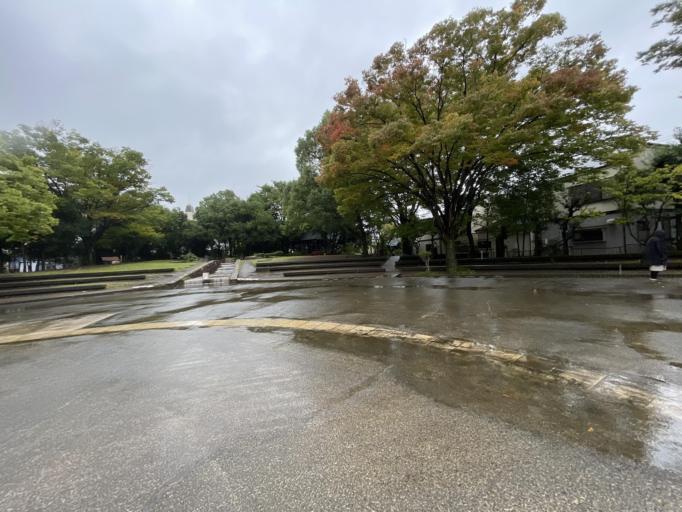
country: JP
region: Kanagawa
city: Zama
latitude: 35.5471
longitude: 139.3291
